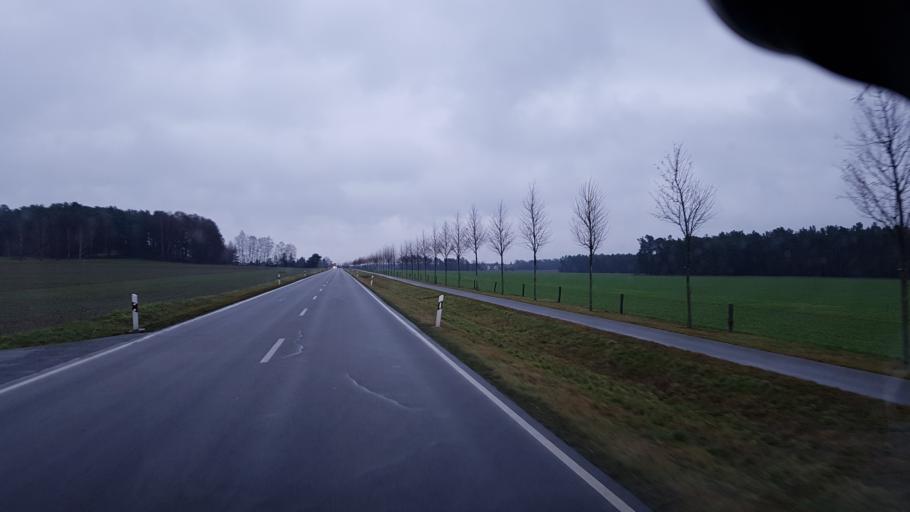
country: DE
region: Brandenburg
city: Sallgast
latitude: 51.6213
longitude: 13.7923
